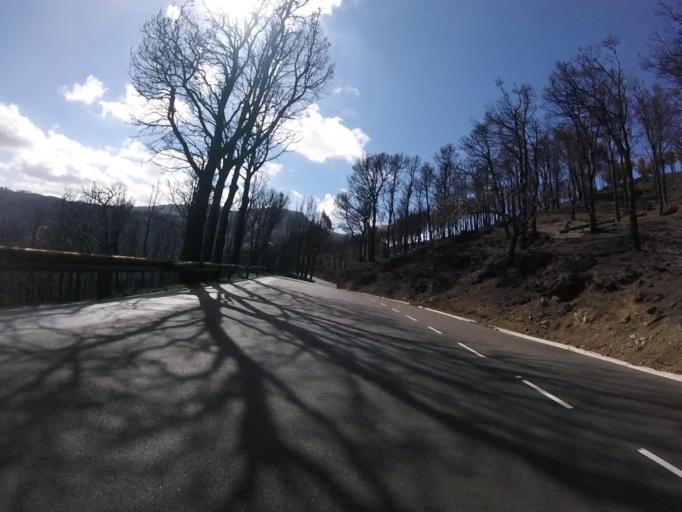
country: ES
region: Canary Islands
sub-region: Provincia de Las Palmas
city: Tejeda
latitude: 27.9943
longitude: -15.5943
